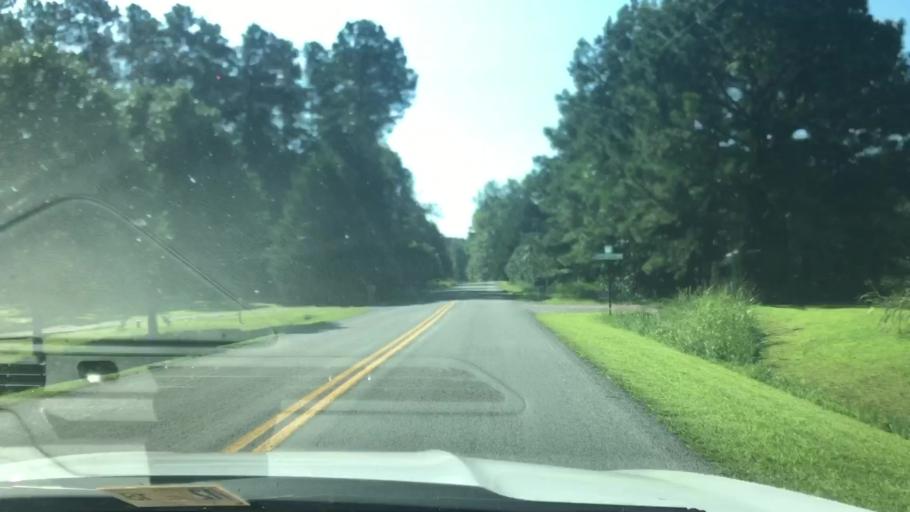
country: US
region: Virginia
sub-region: New Kent County
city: New Kent
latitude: 37.4636
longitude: -76.9283
